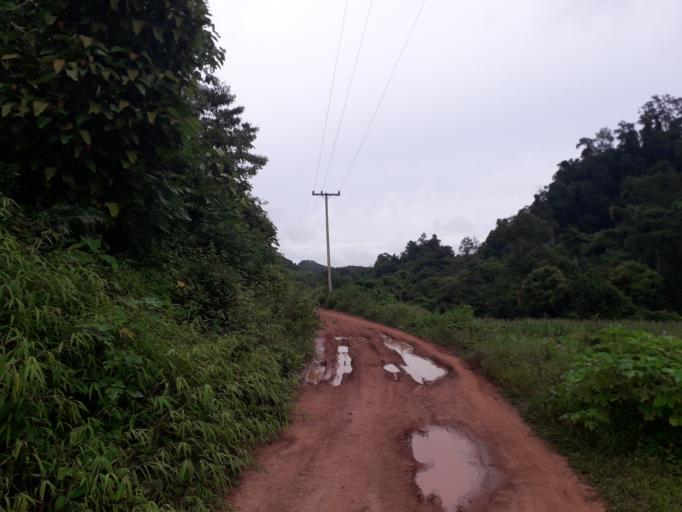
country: CN
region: Yunnan
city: Menglie
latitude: 22.2173
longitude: 101.6515
